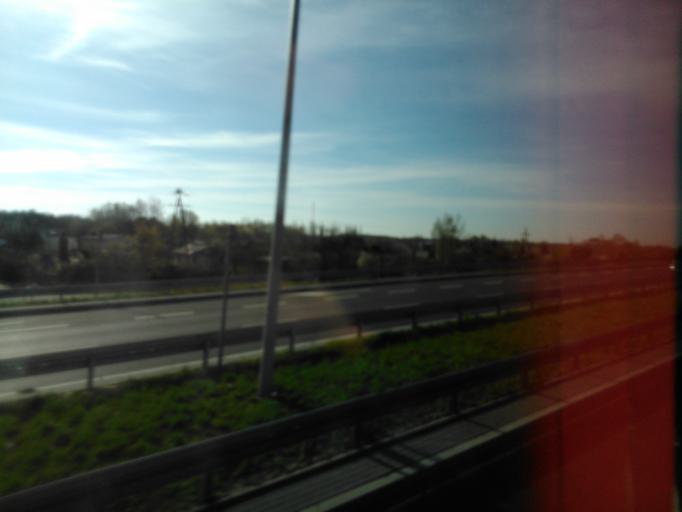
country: PL
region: Kujawsko-Pomorskie
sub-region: Torun
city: Torun
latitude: 52.9999
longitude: 18.6553
